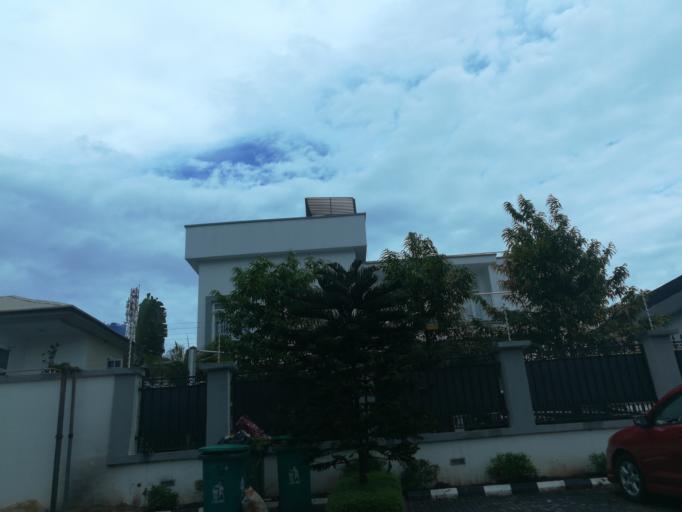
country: NG
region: Lagos
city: Ikoyi
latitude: 6.4394
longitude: 3.4797
